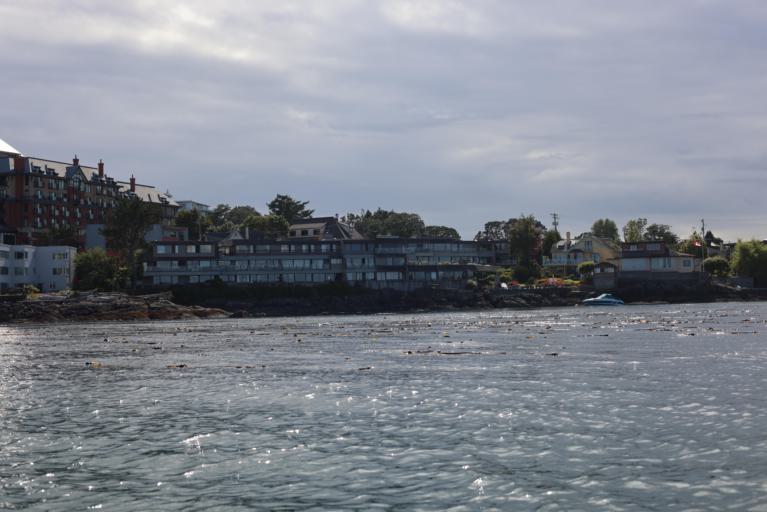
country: CA
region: British Columbia
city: Oak Bay
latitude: 48.4219
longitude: -123.2962
